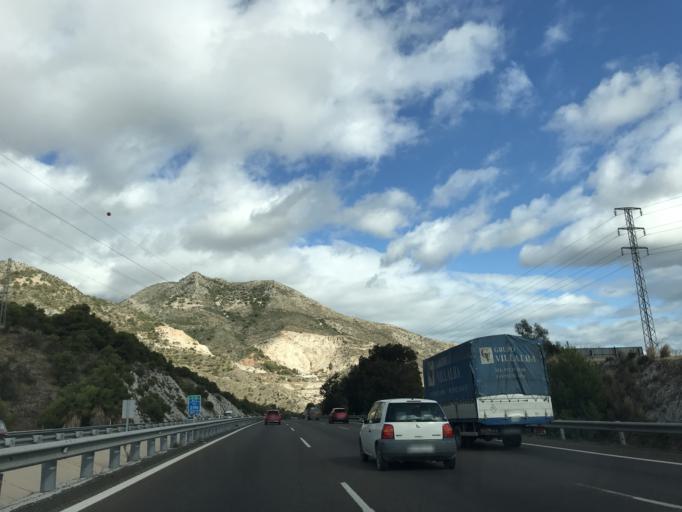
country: ES
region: Andalusia
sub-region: Provincia de Malaga
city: Benalmadena
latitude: 36.5994
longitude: -4.5733
